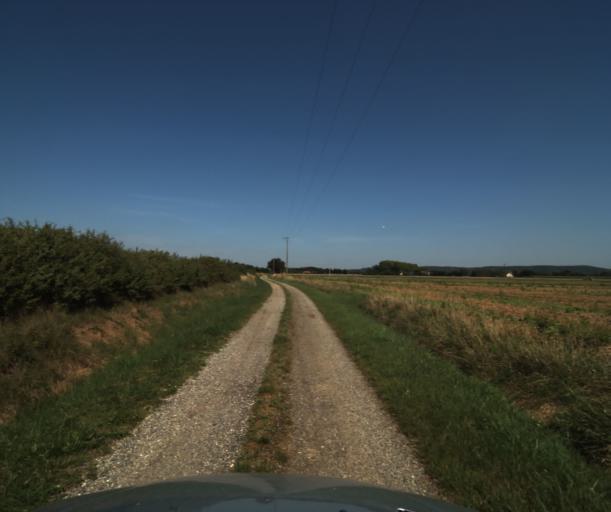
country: FR
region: Midi-Pyrenees
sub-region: Departement de la Haute-Garonne
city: Lacasse
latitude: 43.4341
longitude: 1.2776
